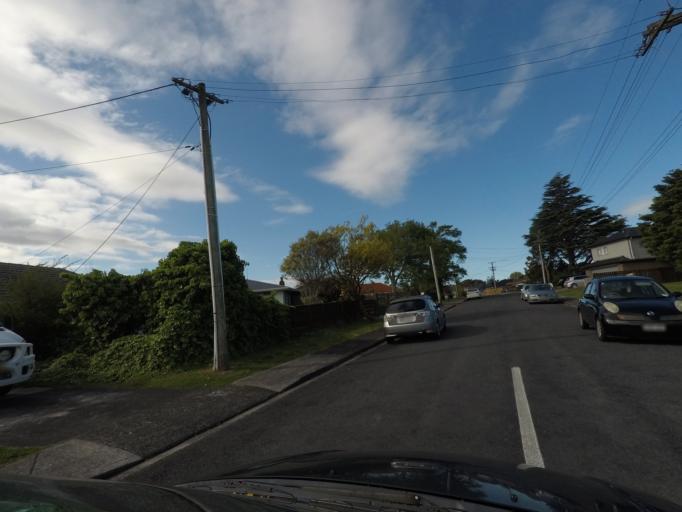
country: NZ
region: Auckland
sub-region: Auckland
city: Rosebank
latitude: -36.8711
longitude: 174.6417
